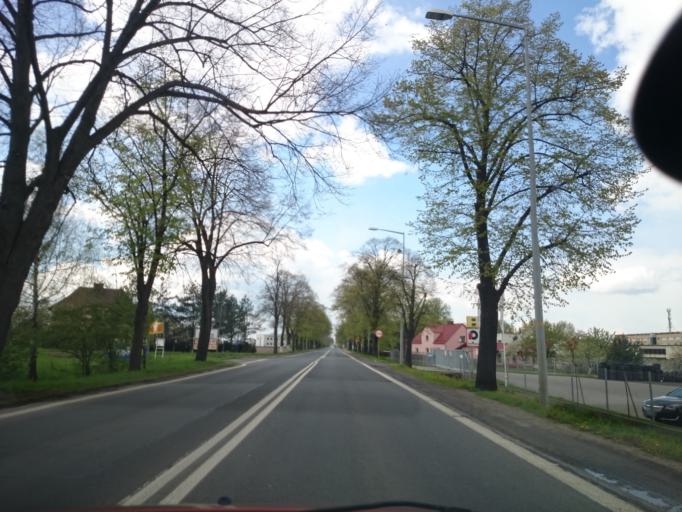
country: PL
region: Opole Voivodeship
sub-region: Powiat opolski
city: Opole
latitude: 50.6488
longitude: 17.9761
